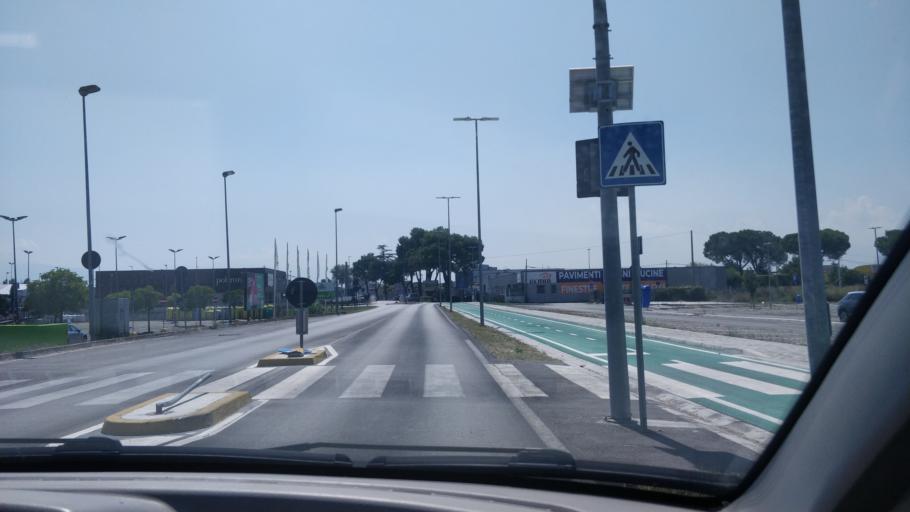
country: IT
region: Abruzzo
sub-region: Provincia di Chieti
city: Sambuceto
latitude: 42.4195
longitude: 14.1746
